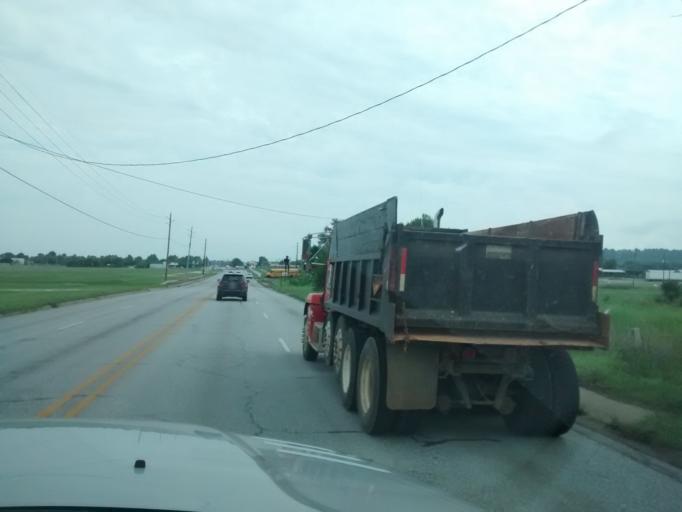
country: US
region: Arkansas
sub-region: Washington County
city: Springdale
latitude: 36.1798
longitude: -94.1164
